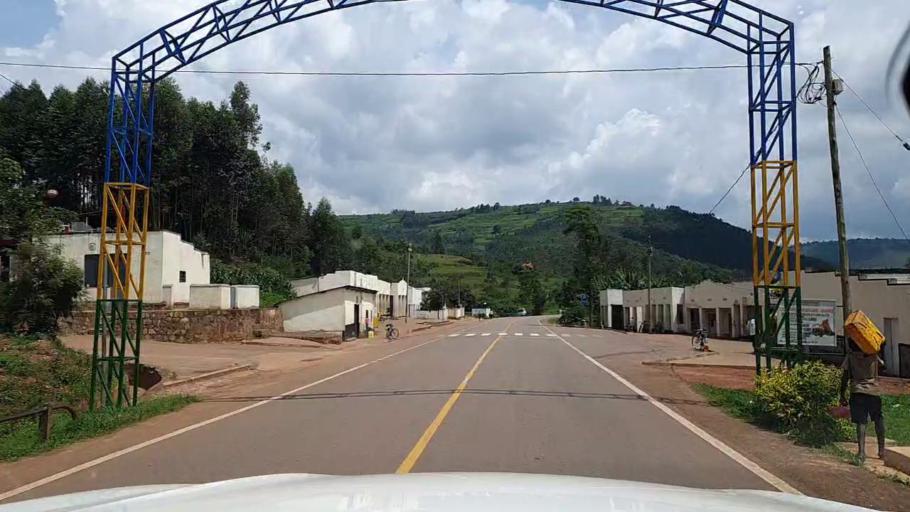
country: RW
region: Kigali
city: Kigali
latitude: -1.8261
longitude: 30.0795
